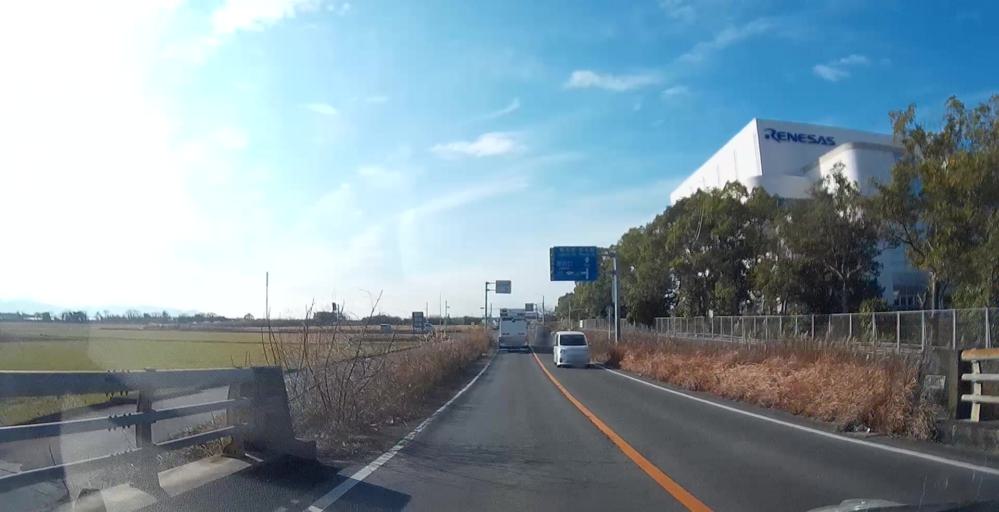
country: JP
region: Kumamoto
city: Uto
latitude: 32.7446
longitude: 130.6776
